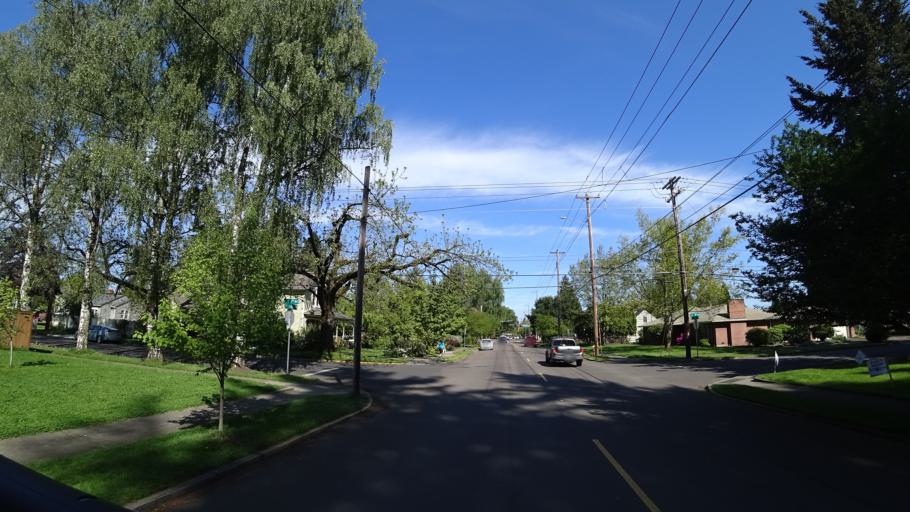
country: US
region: Oregon
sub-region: Washington County
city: Hillsboro
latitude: 45.5223
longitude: -122.9757
